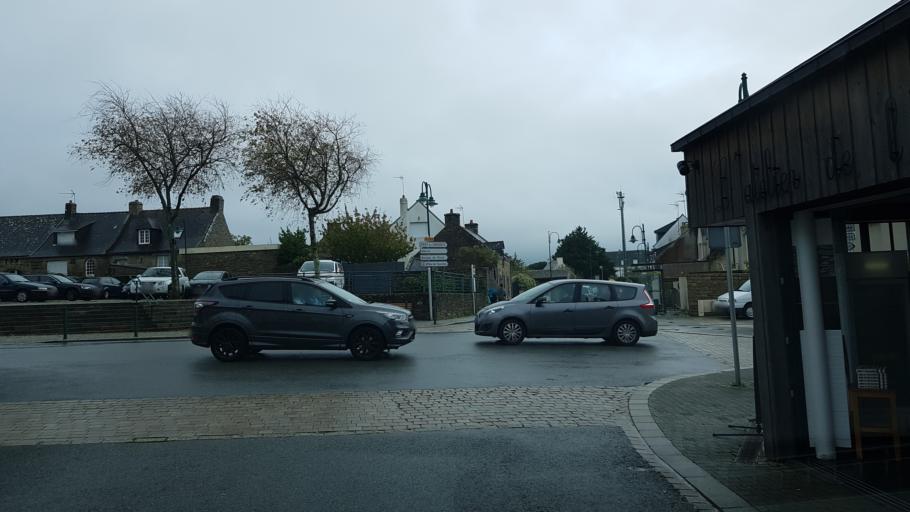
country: FR
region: Brittany
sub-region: Departement du Morbihan
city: Arzon
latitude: 47.5496
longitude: -2.8939
